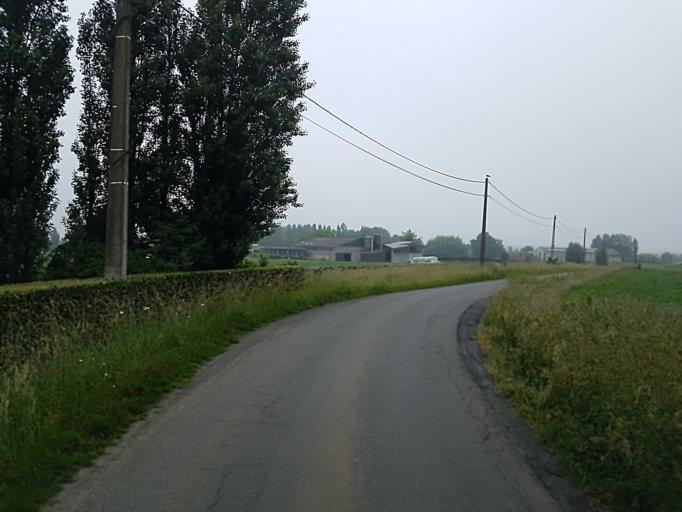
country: BE
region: Flanders
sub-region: Provincie West-Vlaanderen
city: Zonnebeke
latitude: 50.8549
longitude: 2.9783
